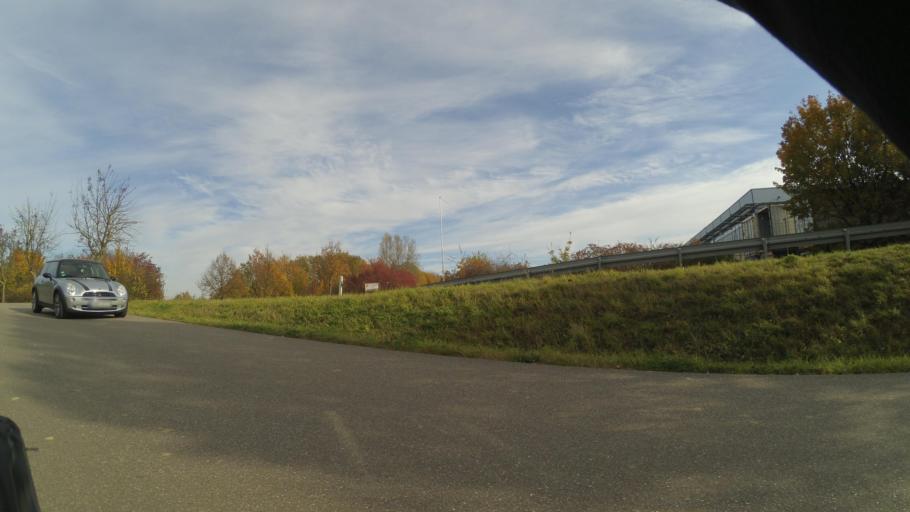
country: DE
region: Baden-Wuerttemberg
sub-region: Regierungsbezirk Stuttgart
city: Ohringen
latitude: 49.2037
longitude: 9.4744
